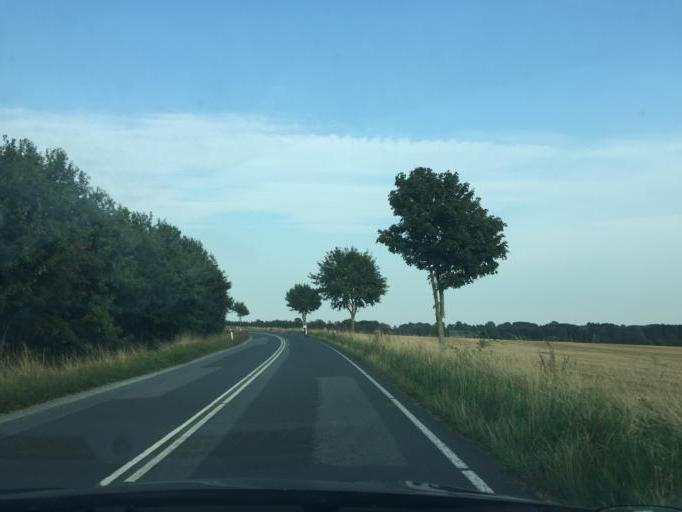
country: DK
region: South Denmark
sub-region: Kerteminde Kommune
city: Langeskov
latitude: 55.2872
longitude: 10.5503
